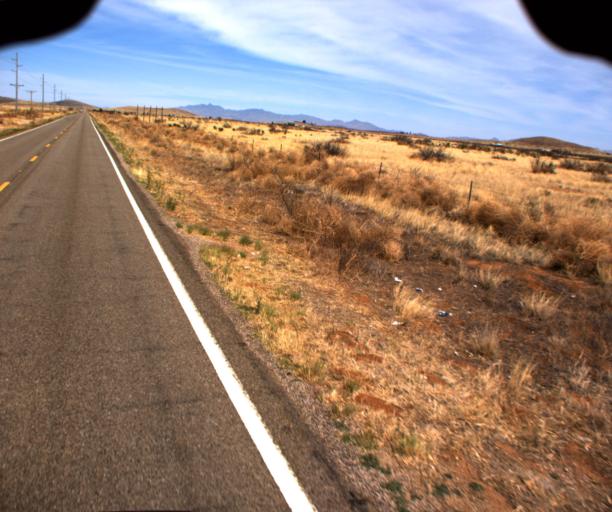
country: US
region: Arizona
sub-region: Cochise County
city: Tombstone
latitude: 31.8564
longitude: -109.6951
